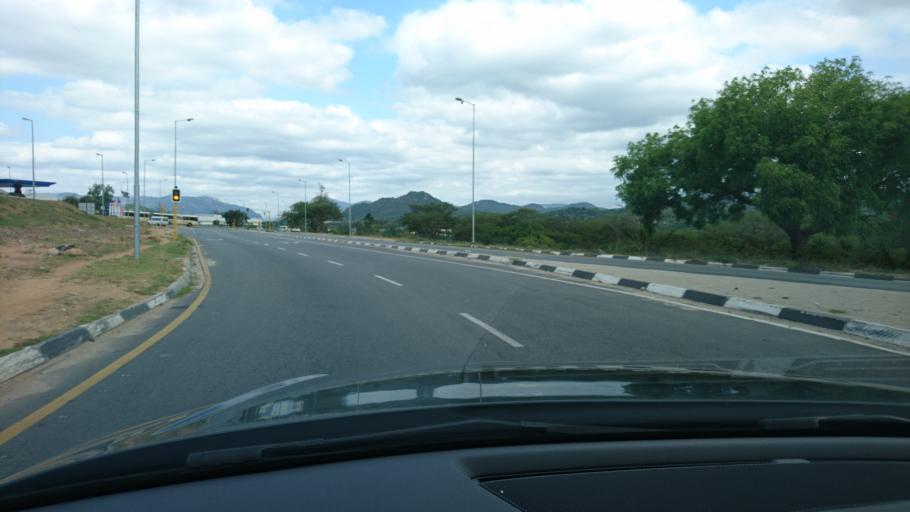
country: ZA
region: Mpumalanga
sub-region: Ehlanzeni District
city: Nelspruit
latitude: -25.4668
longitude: 31.0915
